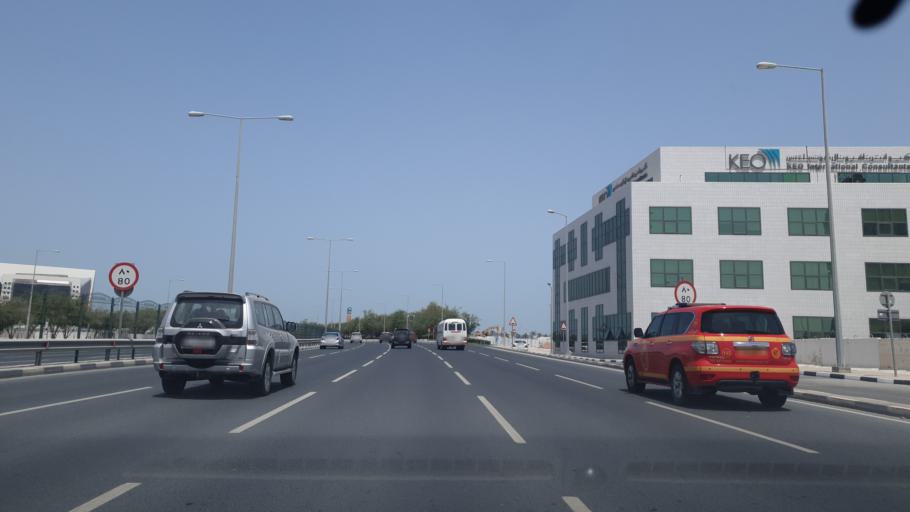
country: QA
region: Baladiyat ad Dawhah
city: Doha
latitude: 25.2686
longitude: 51.5509
